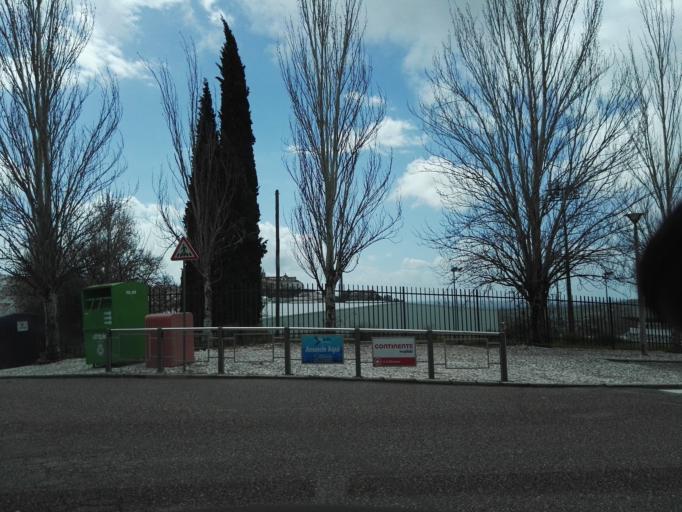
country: PT
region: Portalegre
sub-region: Portalegre
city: Portalegre
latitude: 39.2991
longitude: -7.4324
